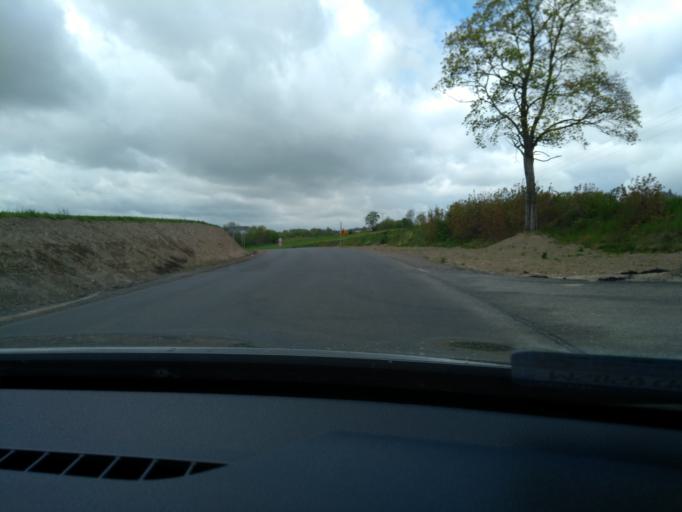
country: PL
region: Pomeranian Voivodeship
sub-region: Powiat kartuski
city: Chmielno
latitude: 54.3429
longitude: 18.0507
